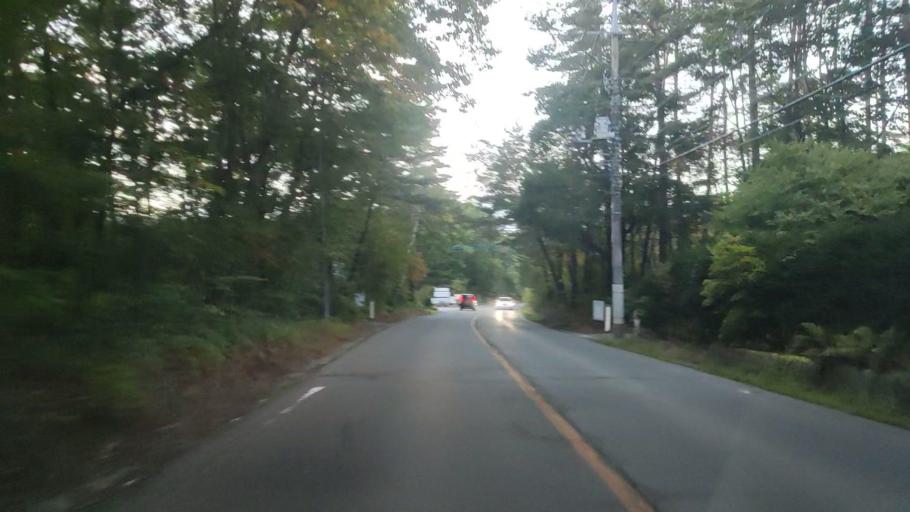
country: JP
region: Nagano
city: Komoro
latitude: 36.4462
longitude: 138.5798
